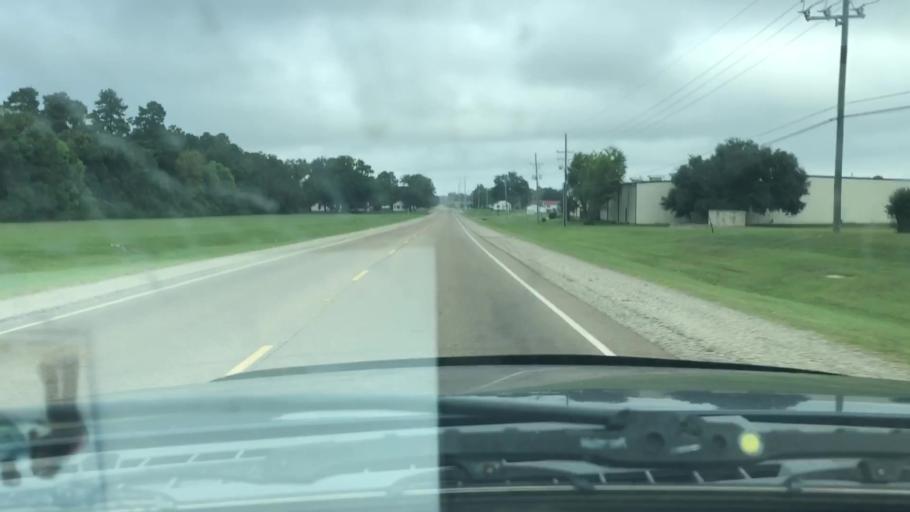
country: US
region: Texas
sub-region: Bowie County
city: Wake Village
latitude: 33.3779
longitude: -94.0922
